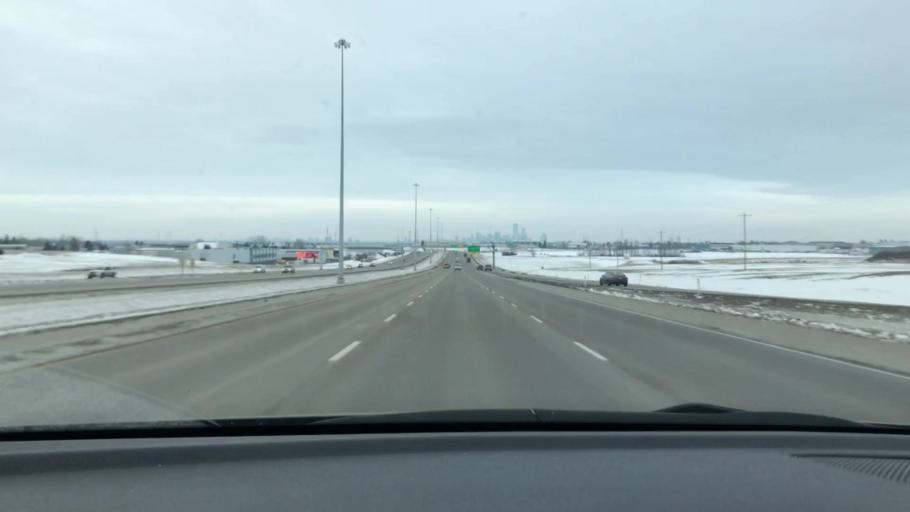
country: CA
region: Alberta
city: Sherwood Park
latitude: 53.5140
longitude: -113.3494
